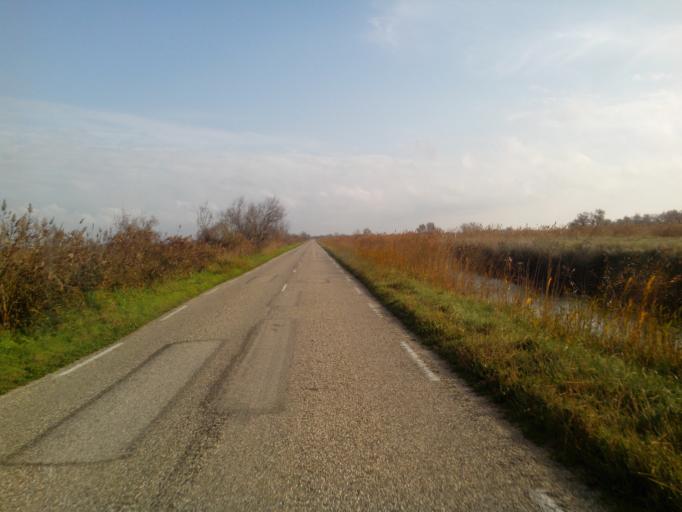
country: FR
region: Languedoc-Roussillon
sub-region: Departement du Gard
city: Saint-Gilles
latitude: 43.5789
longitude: 4.5158
